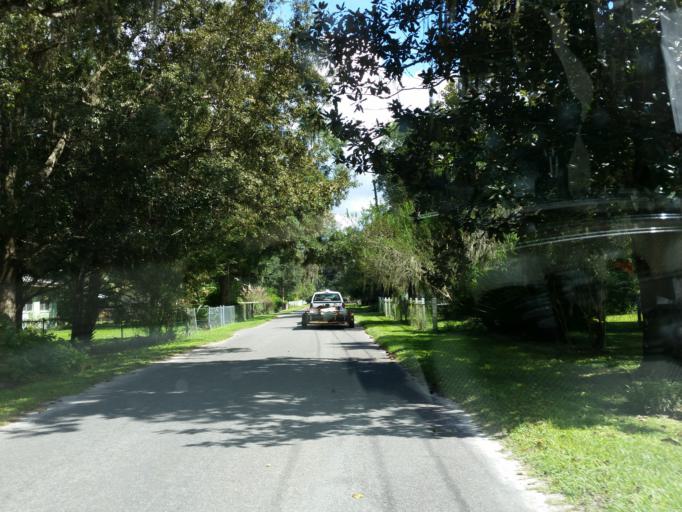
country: US
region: Florida
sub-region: Alachua County
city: Gainesville
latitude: 29.5045
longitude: -82.2830
